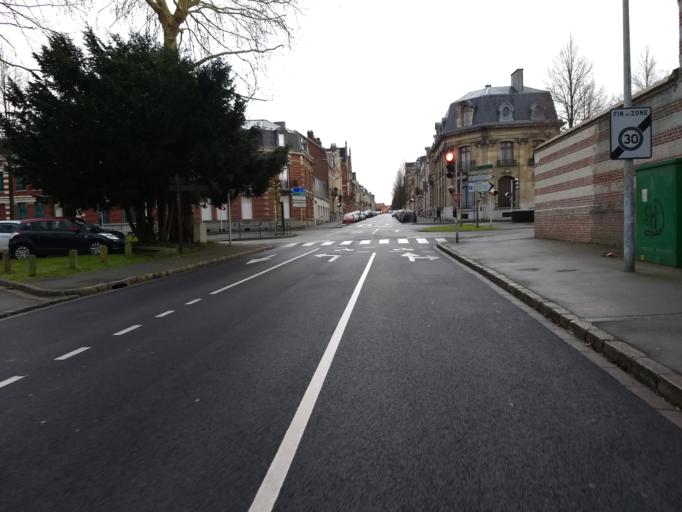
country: FR
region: Nord-Pas-de-Calais
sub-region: Departement du Pas-de-Calais
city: Arras
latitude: 50.2877
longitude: 2.7711
